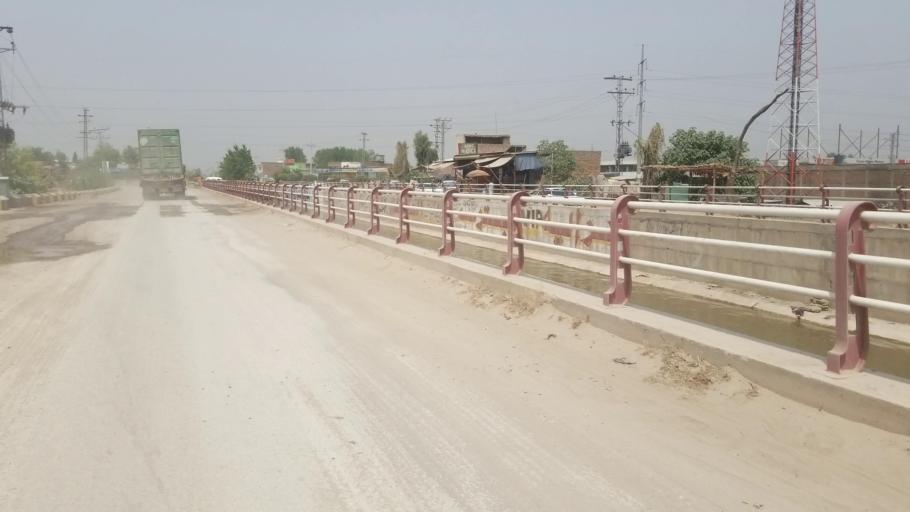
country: PK
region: Khyber Pakhtunkhwa
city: Peshawar
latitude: 33.9681
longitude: 71.5390
